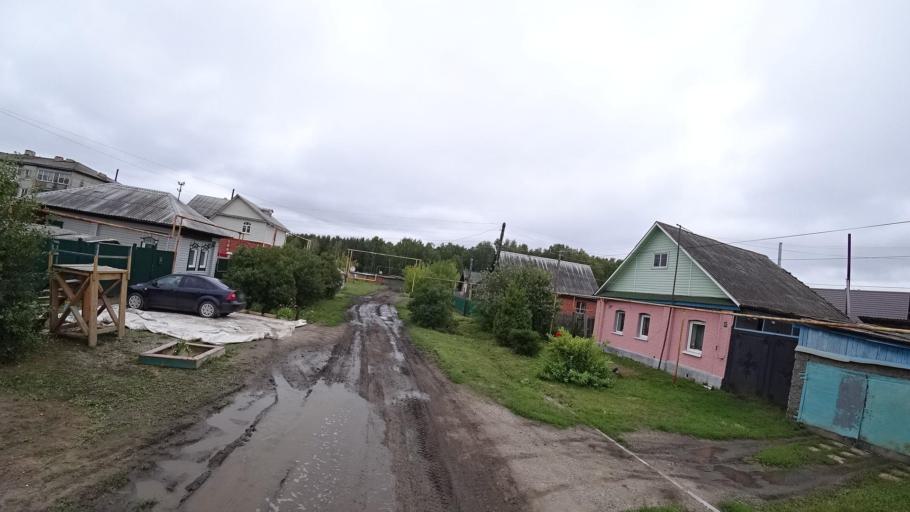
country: RU
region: Sverdlovsk
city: Kamyshlov
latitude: 56.8440
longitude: 62.7546
